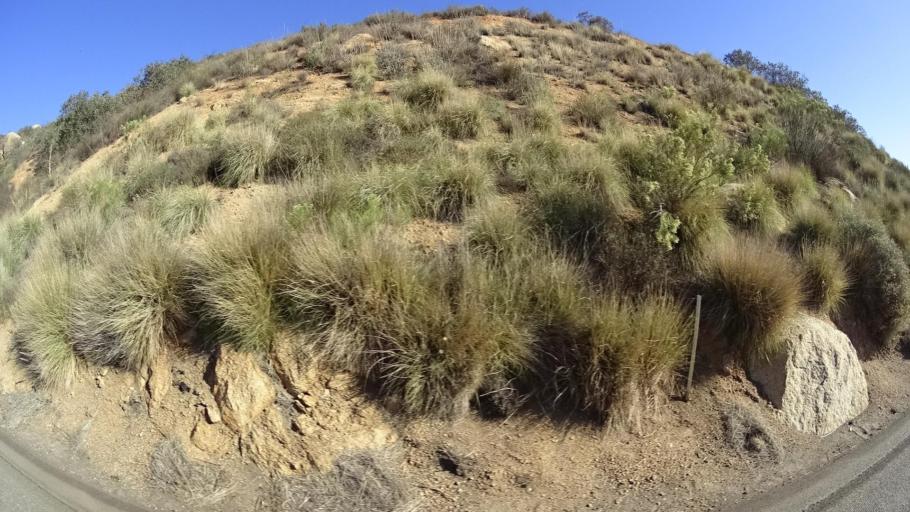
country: MX
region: Baja California
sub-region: Tecate
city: Lomas de Santa Anita
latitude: 32.6155
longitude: -116.7244
